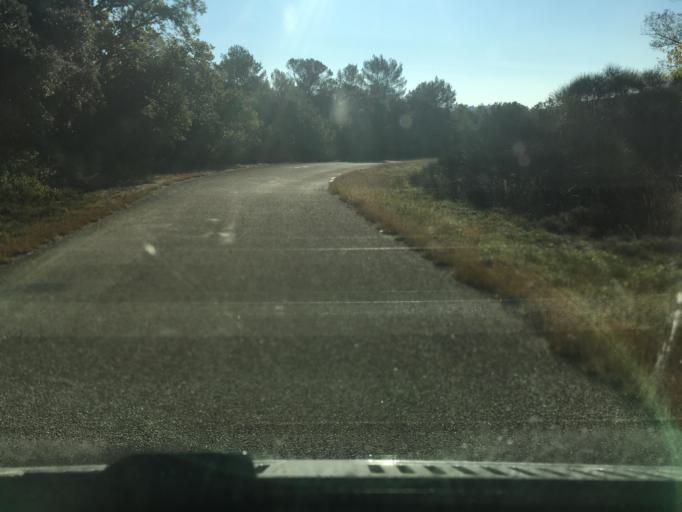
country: FR
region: Languedoc-Roussillon
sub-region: Departement du Gard
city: Goudargues
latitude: 44.1657
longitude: 4.3515
